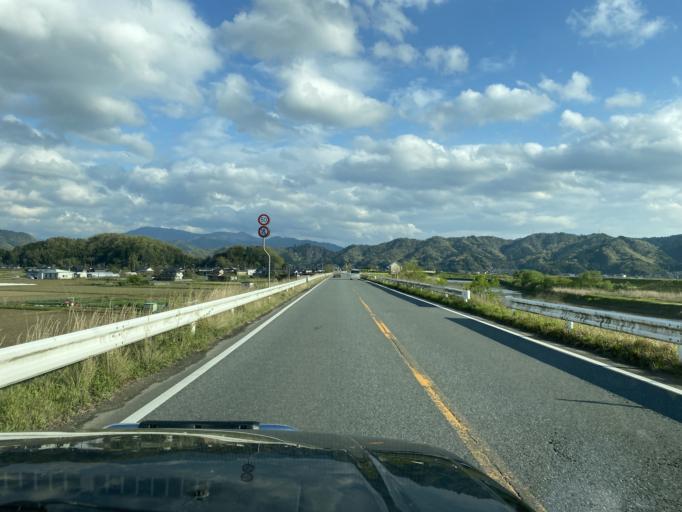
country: JP
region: Hyogo
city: Toyooka
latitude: 35.4994
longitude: 134.8395
